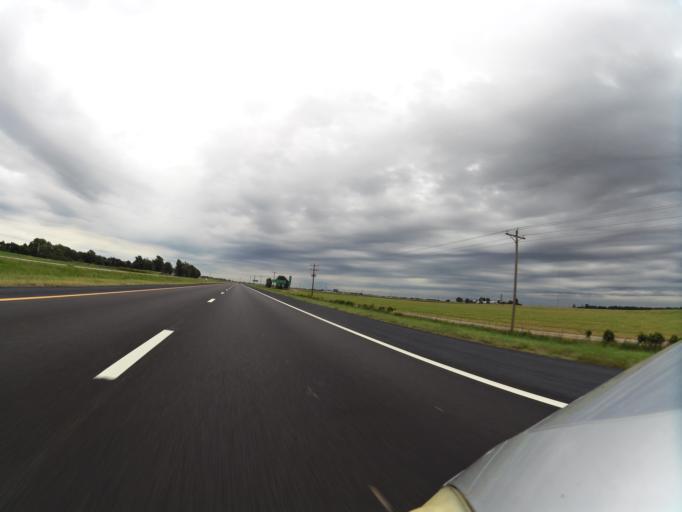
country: US
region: Kansas
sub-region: Sedgwick County
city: Colwich
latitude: 37.8252
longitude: -97.5419
